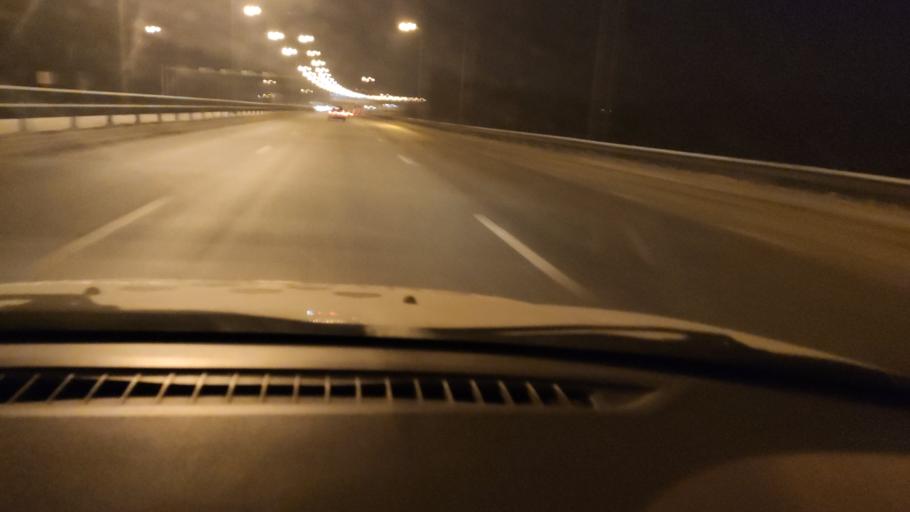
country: RU
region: Perm
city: Bershet'
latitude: 57.6952
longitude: 56.3900
